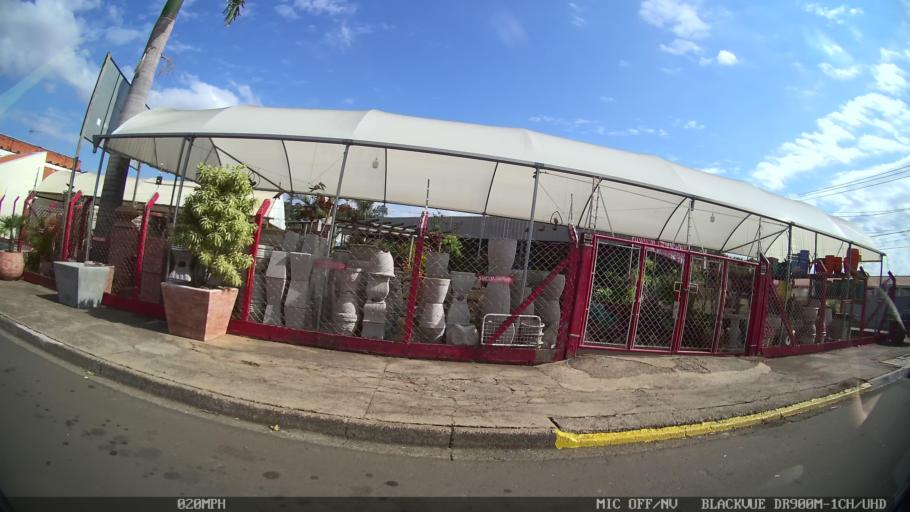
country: BR
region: Sao Paulo
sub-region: Americana
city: Americana
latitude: -22.7305
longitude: -47.3137
